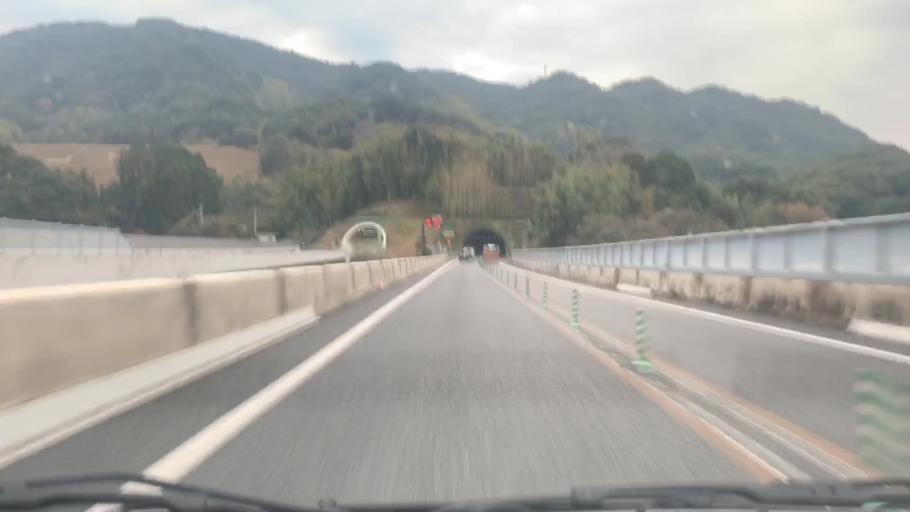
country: JP
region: Nagasaki
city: Obita
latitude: 32.8004
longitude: 129.9650
